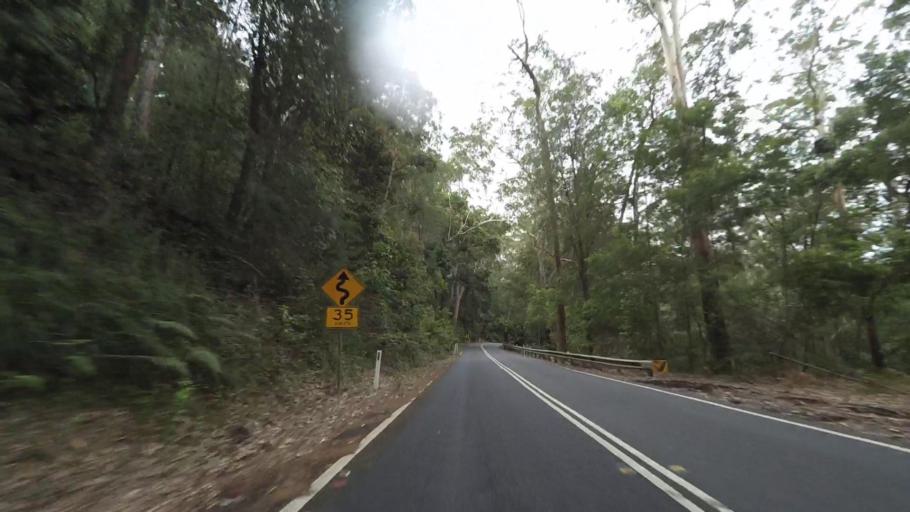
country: AU
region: New South Wales
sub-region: Wollongong
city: Helensburgh
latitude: -34.1515
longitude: 151.0328
